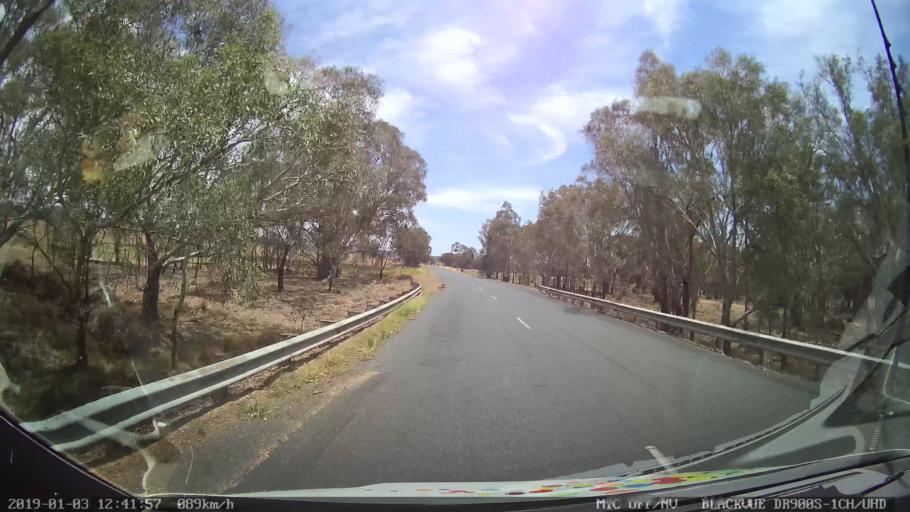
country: AU
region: New South Wales
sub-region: Weddin
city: Grenfell
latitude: -33.7929
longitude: 148.2148
